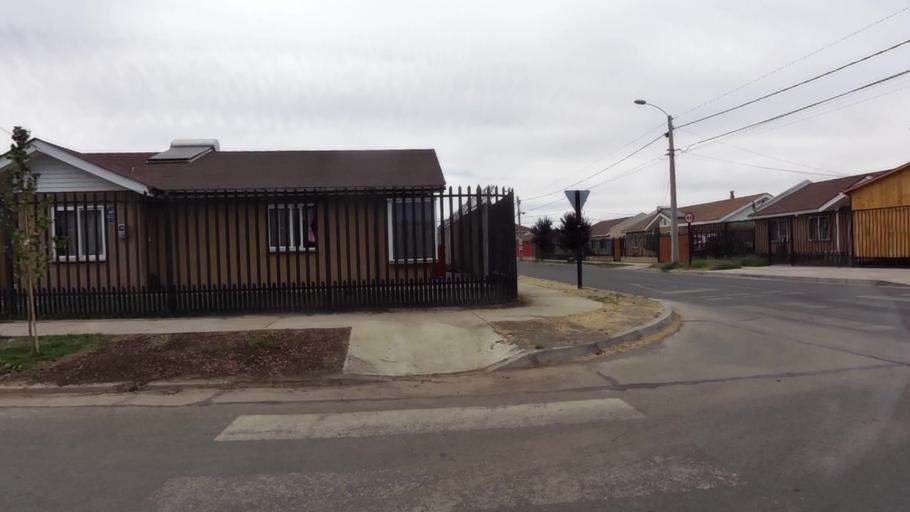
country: CL
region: O'Higgins
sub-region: Provincia de Cachapoal
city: Graneros
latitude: -34.0800
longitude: -70.7372
